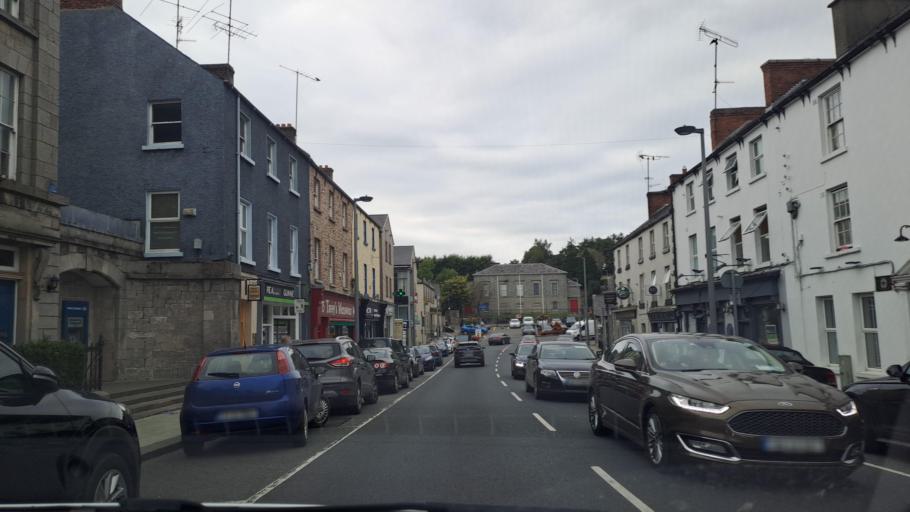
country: IE
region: Ulster
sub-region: County Monaghan
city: Carrickmacross
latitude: 53.9769
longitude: -6.7197
